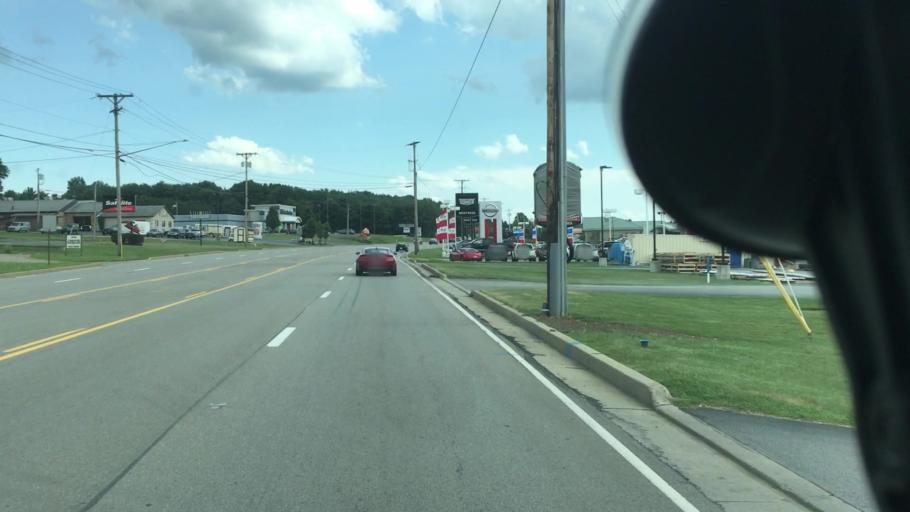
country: US
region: Pennsylvania
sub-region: Mercer County
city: Hermitage
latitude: 41.2534
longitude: -80.4513
